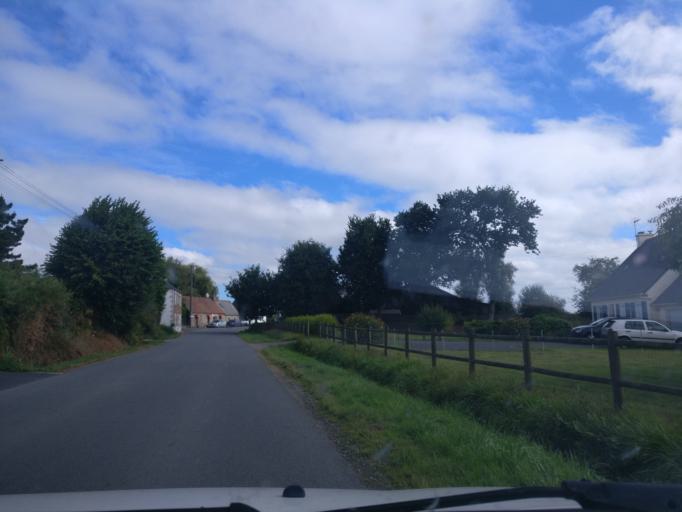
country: FR
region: Brittany
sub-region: Departement des Cotes-d'Armor
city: Rospez
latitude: 48.7334
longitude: -3.3789
